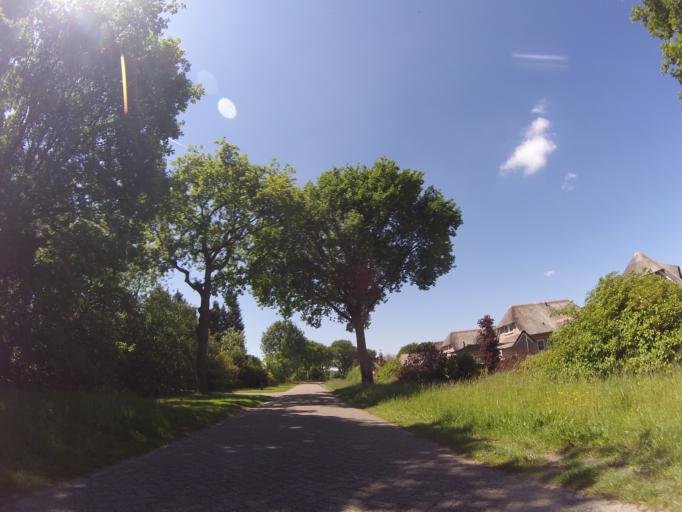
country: NL
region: Drenthe
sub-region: Gemeente Hoogeveen
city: Hoogeveen
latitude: 52.7604
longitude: 6.5557
